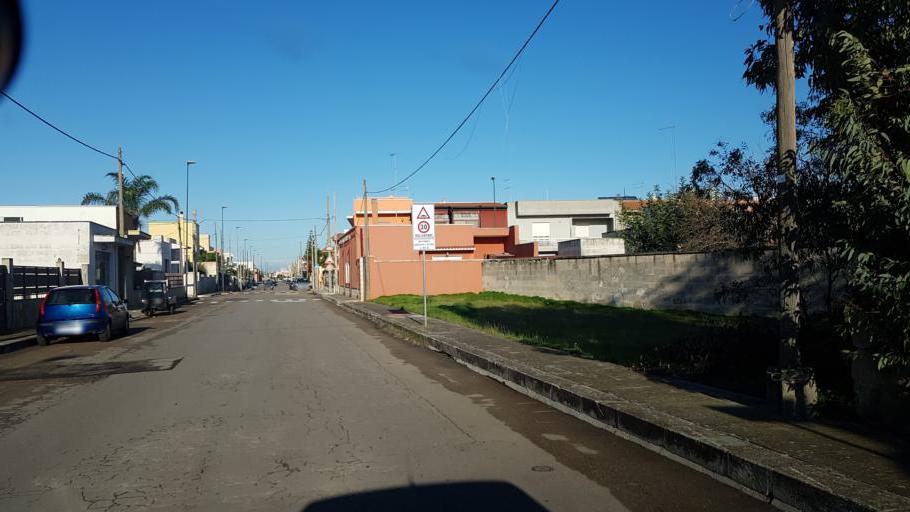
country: IT
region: Apulia
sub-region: Provincia di Brindisi
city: Torchiarolo
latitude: 40.4808
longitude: 18.0519
